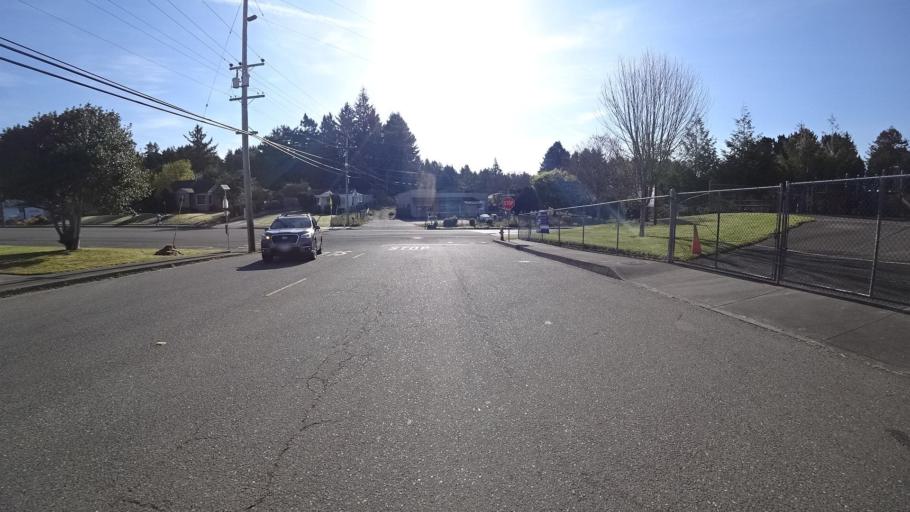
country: US
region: California
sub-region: Humboldt County
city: Cutten
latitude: 40.7712
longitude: -124.1619
